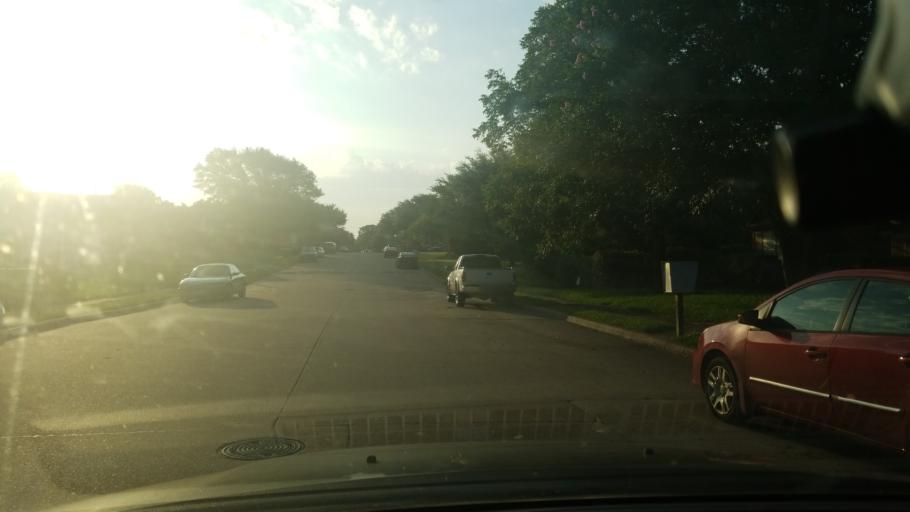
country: US
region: Texas
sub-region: Dallas County
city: Balch Springs
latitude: 32.7255
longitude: -96.6537
